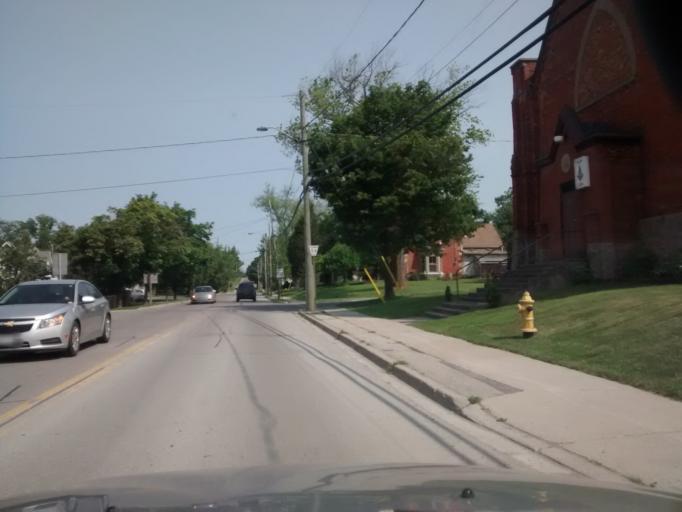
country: CA
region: Ontario
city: Ancaster
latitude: 42.9509
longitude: -79.8559
